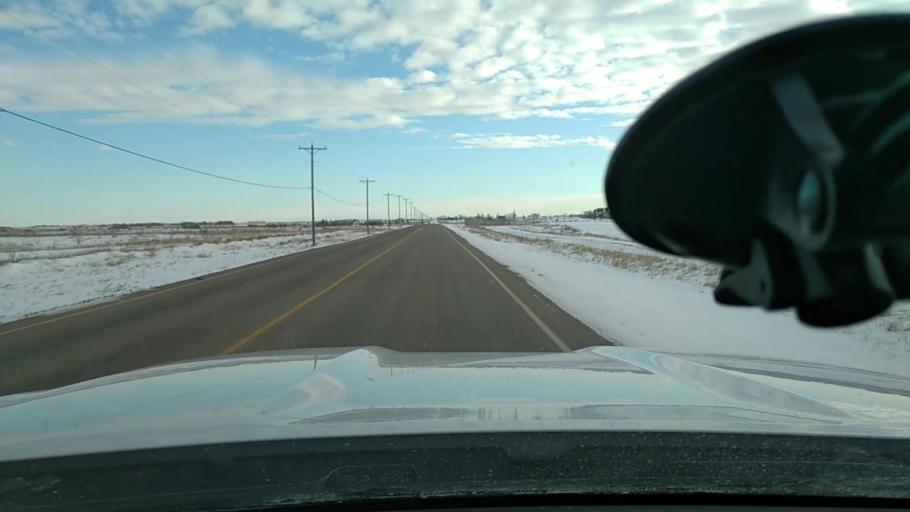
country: CA
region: Alberta
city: Chestermere
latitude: 50.9651
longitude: -113.6716
